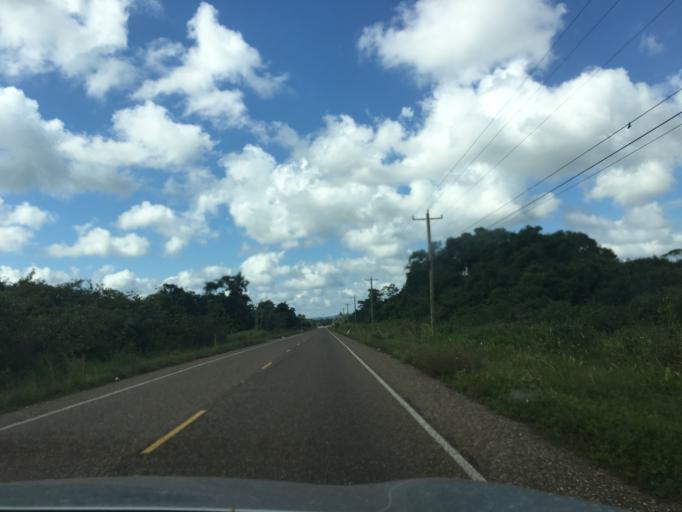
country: BZ
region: Stann Creek
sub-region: Dangriga
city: Dangriga
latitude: 16.8580
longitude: -88.3034
